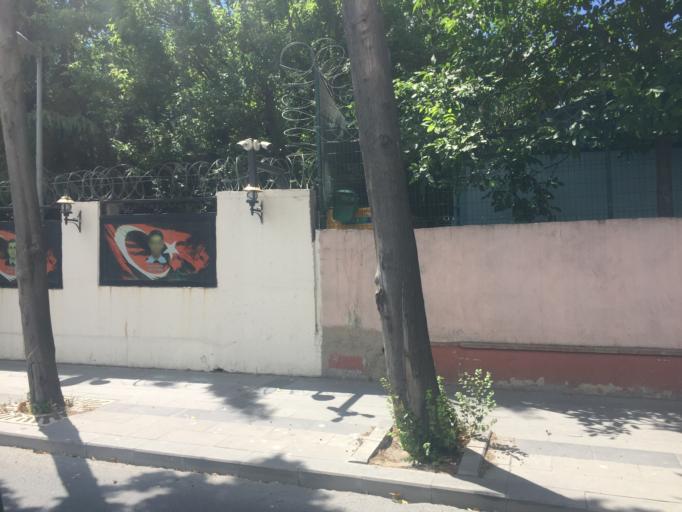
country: TR
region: Istanbul
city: merter keresteciler
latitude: 41.0330
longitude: 28.9123
